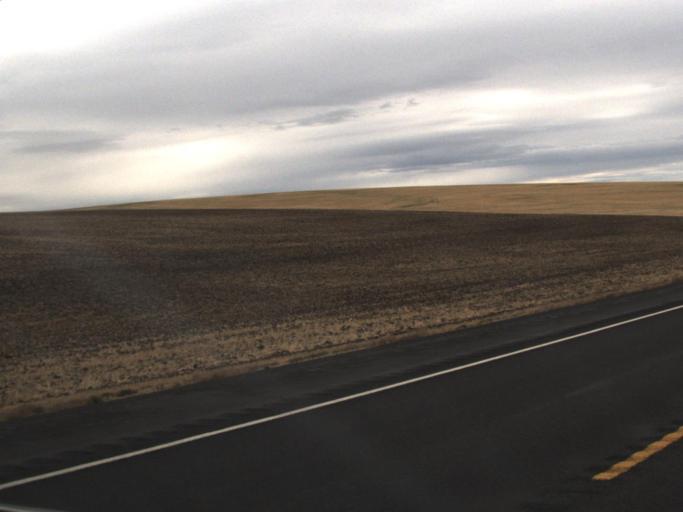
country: US
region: Washington
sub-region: Asotin County
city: Clarkston
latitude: 46.5041
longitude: -117.0786
